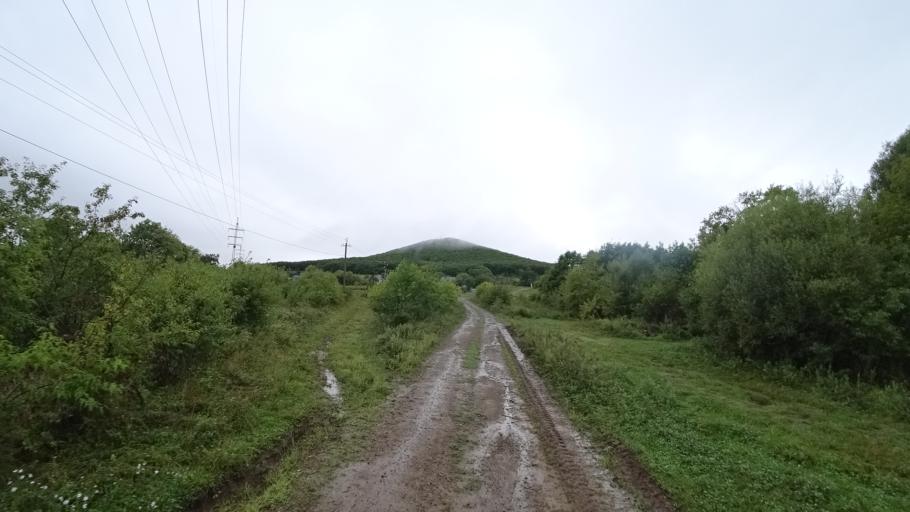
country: RU
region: Primorskiy
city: Monastyrishche
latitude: 44.2636
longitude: 132.4242
